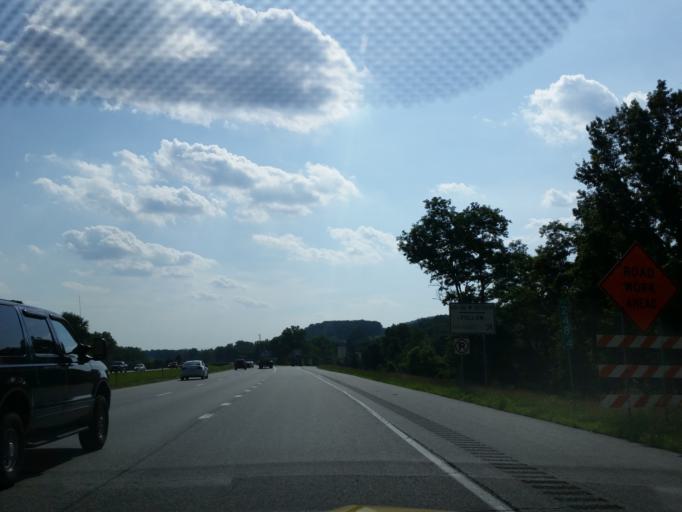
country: US
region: Pennsylvania
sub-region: York County
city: Hallam
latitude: 40.0070
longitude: -76.6115
